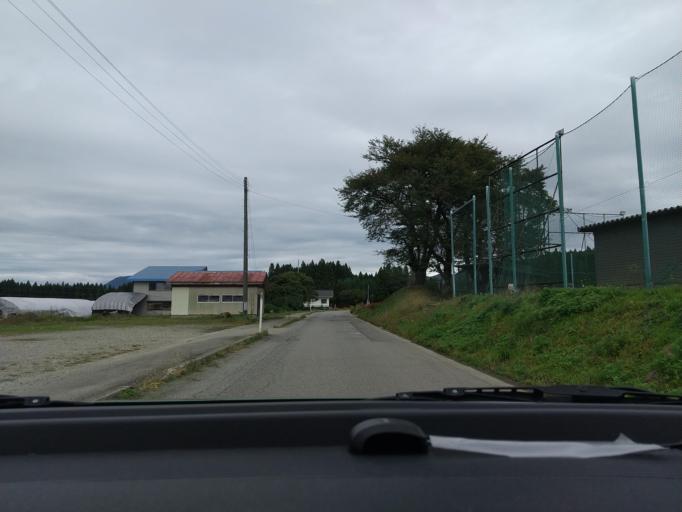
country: JP
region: Akita
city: Kakunodatemachi
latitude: 39.5881
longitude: 140.6079
